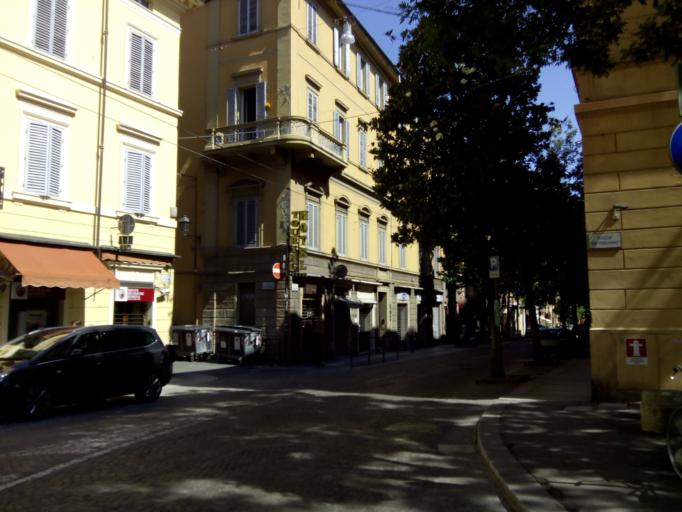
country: IT
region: Emilia-Romagna
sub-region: Provincia di Bologna
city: Bologna
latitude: 44.4885
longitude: 11.3432
